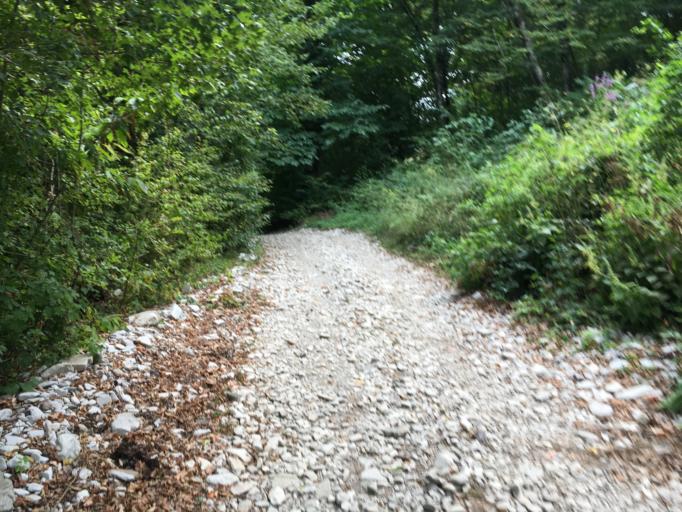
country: RU
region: Krasnodarskiy
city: Tuapse
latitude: 44.2638
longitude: 39.2138
